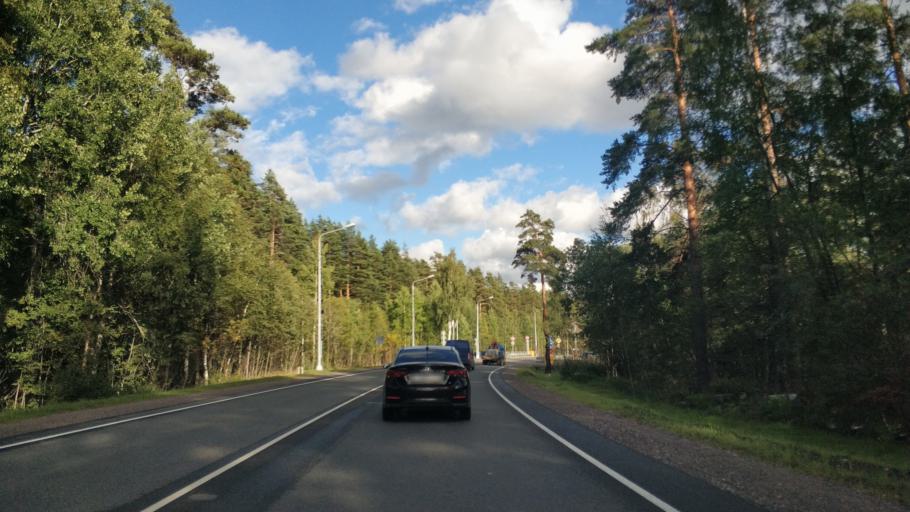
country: RU
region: Leningrad
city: Priozersk
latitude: 61.0092
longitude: 30.1686
